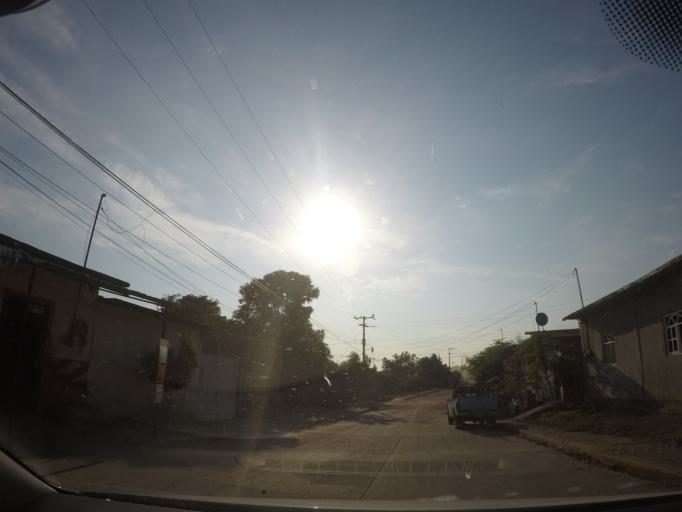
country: MX
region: Oaxaca
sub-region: Santo Domingo Tehuantepec
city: La Noria
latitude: 16.2467
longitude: -95.1450
